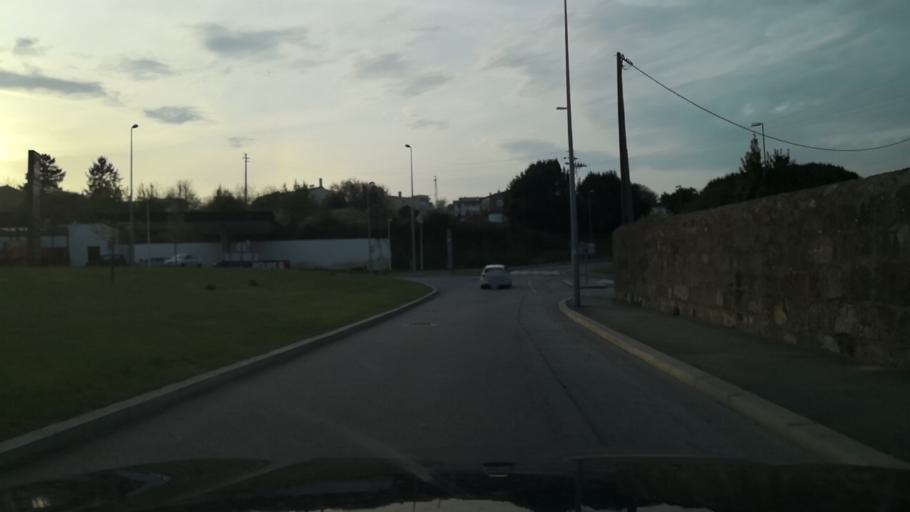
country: PT
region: Porto
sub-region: Maia
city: Leca do Bailio
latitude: 41.2057
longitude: -8.6202
